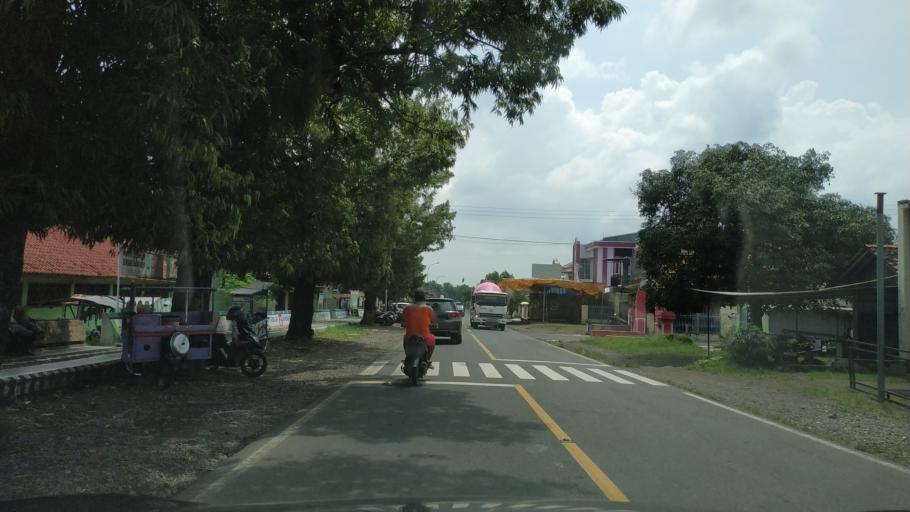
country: ID
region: Central Java
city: Lebaksiu
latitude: -7.0452
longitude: 109.1467
